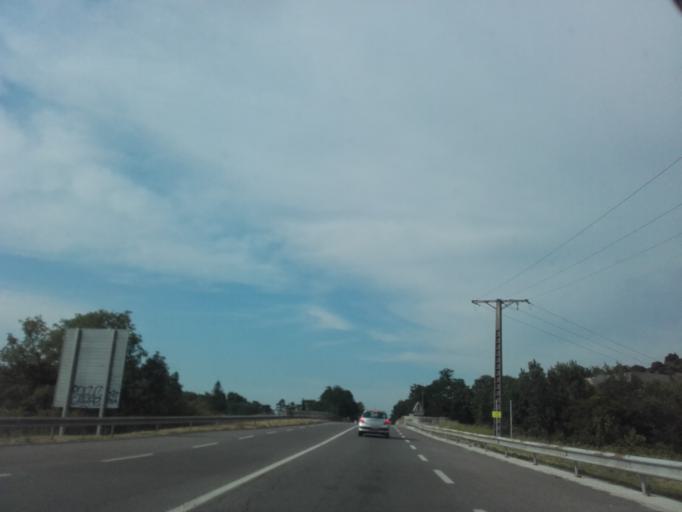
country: FR
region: Rhone-Alpes
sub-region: Departement de la Drome
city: Livron-sur-Drome
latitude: 44.7646
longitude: 4.8397
